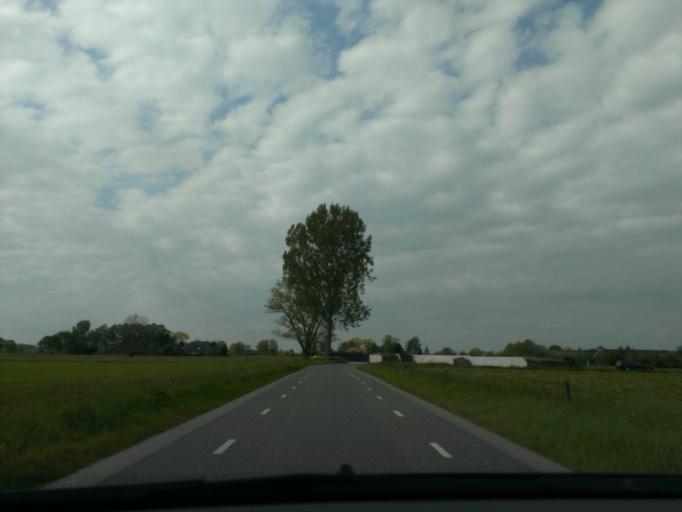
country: NL
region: Gelderland
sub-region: Gemeente Voorst
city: Twello
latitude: 52.2515
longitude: 6.0598
